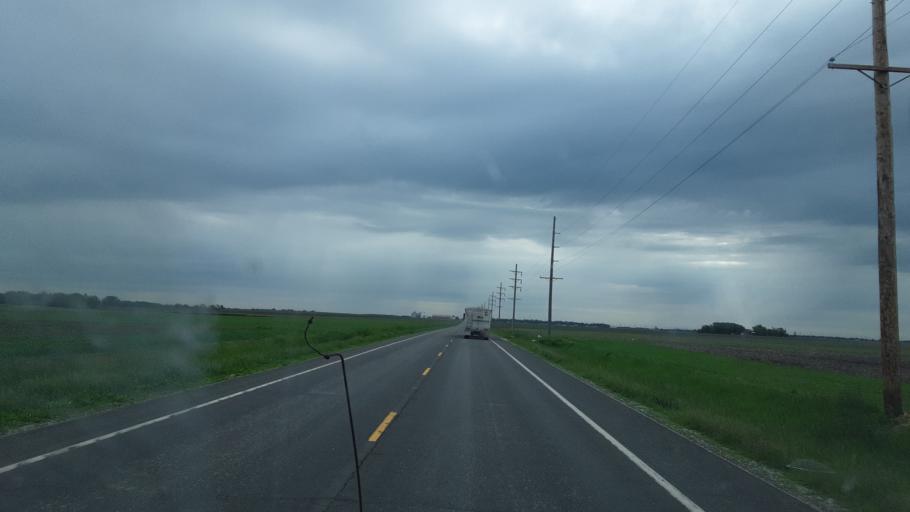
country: US
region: Illinois
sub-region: Fulton County
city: Astoria
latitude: 40.3564
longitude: -90.3777
